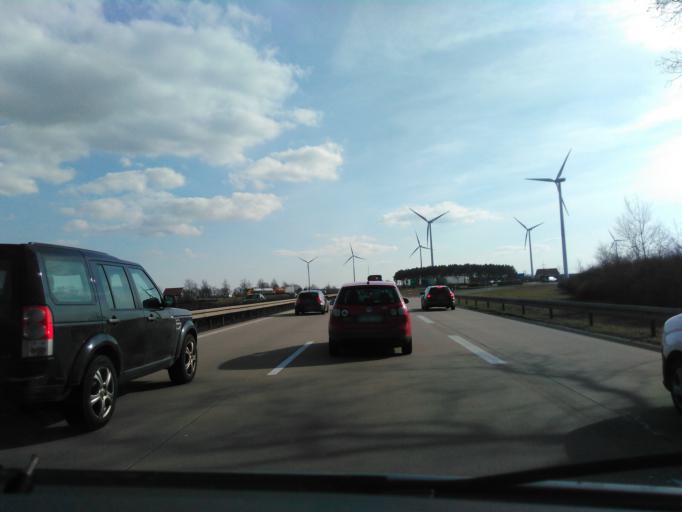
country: DE
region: Brandenburg
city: Kasel-Golzig
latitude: 51.9966
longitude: 13.7241
